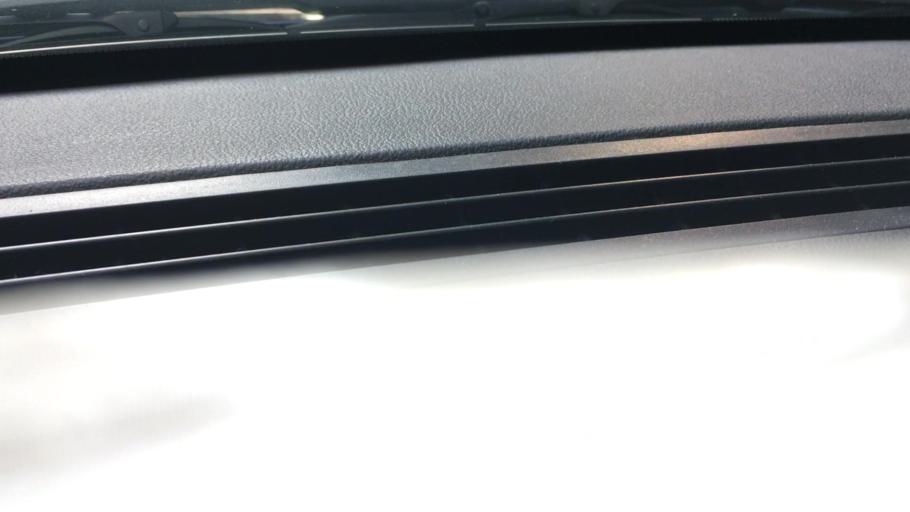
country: US
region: Alabama
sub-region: Shelby County
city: Helena
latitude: 33.2449
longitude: -86.9563
